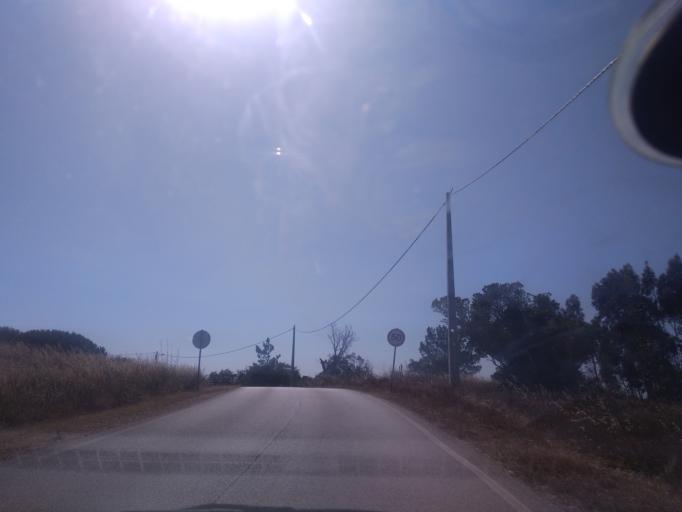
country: PT
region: Faro
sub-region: Aljezur
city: Aljezur
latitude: 37.2276
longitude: -8.8168
